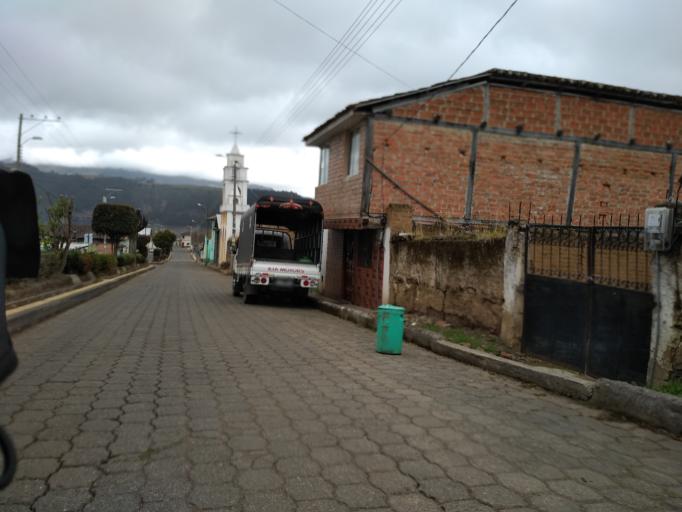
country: EC
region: Carchi
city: El Angel
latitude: 0.6248
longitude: -77.9359
